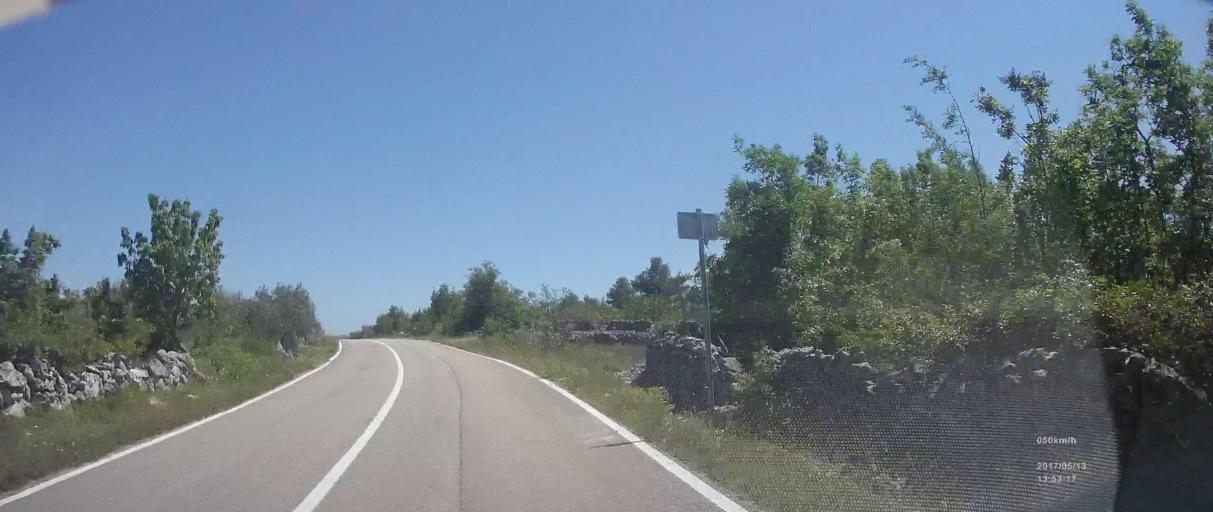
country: HR
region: Sibensko-Kniniska
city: Primosten
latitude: 43.6003
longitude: 15.9971
